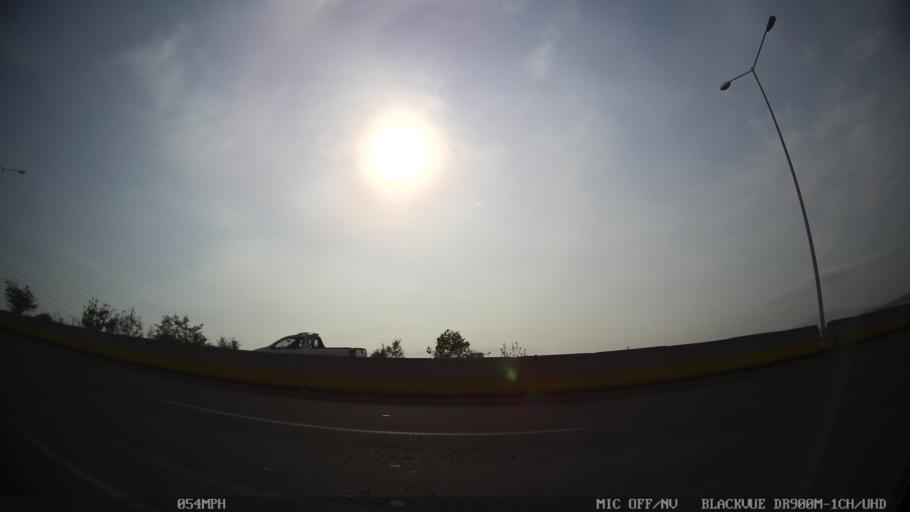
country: MX
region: Jalisco
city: Coyula
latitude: 20.6484
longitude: -103.2046
